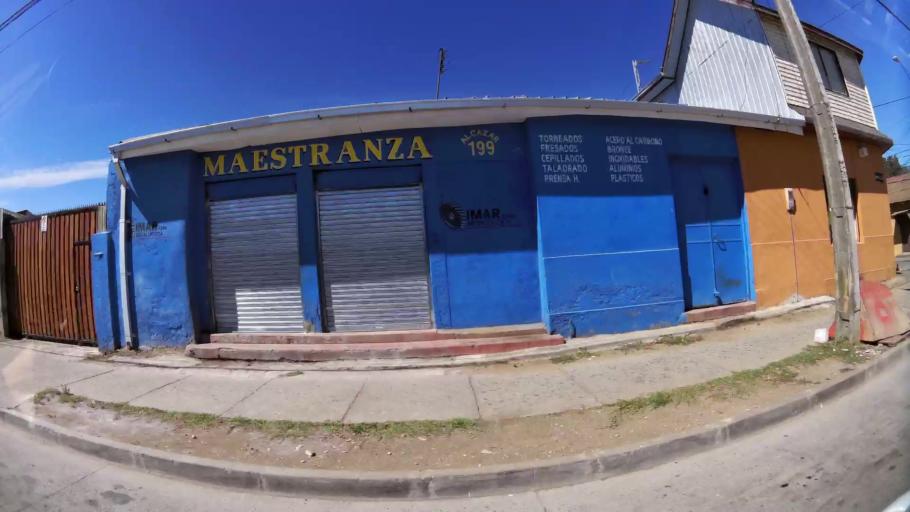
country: CL
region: Biobio
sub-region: Provincia de Concepcion
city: Penco
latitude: -36.7344
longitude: -72.9906
